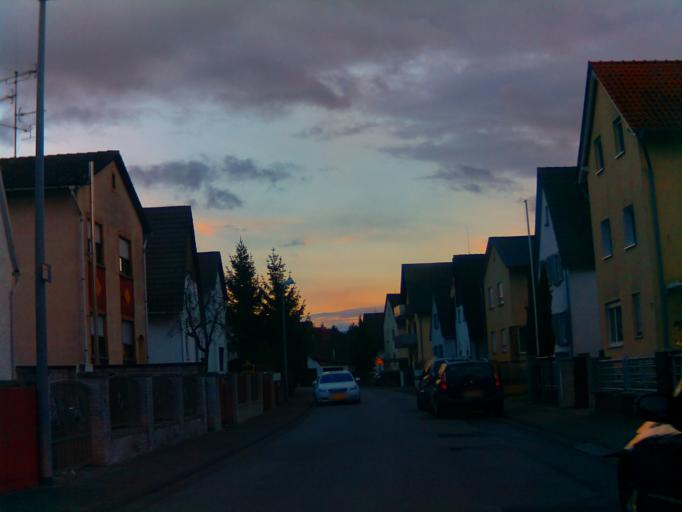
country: DE
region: Hesse
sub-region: Regierungsbezirk Darmstadt
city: Gross-Rohrheim
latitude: 49.7138
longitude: 8.4710
